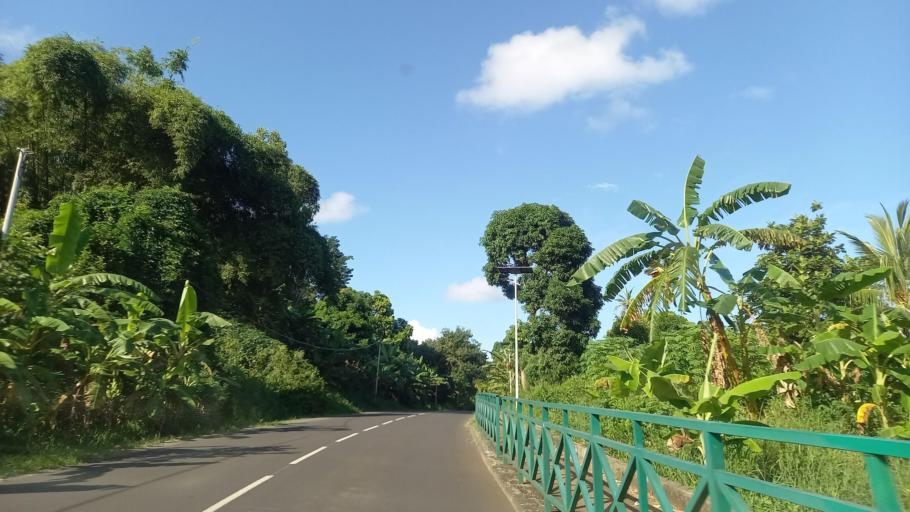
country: YT
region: Kani-Keli
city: Kani Keli
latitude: -12.9583
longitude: 45.1133
